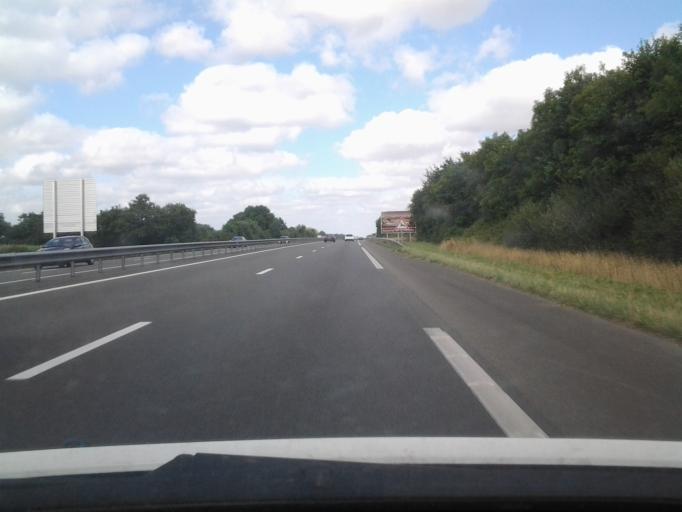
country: FR
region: Pays de la Loire
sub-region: Departement de la Vendee
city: Sainte-Flaive-des-Loups
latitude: 46.6312
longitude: -1.5692
